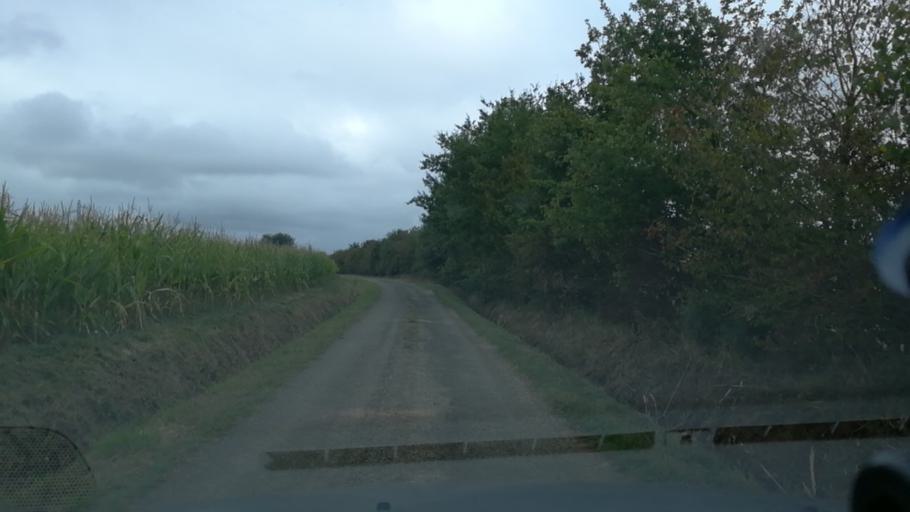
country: FR
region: Brittany
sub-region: Departement d'Ille-et-Vilaine
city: Vezin-le-Coquet
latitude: 48.1133
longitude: -1.7298
